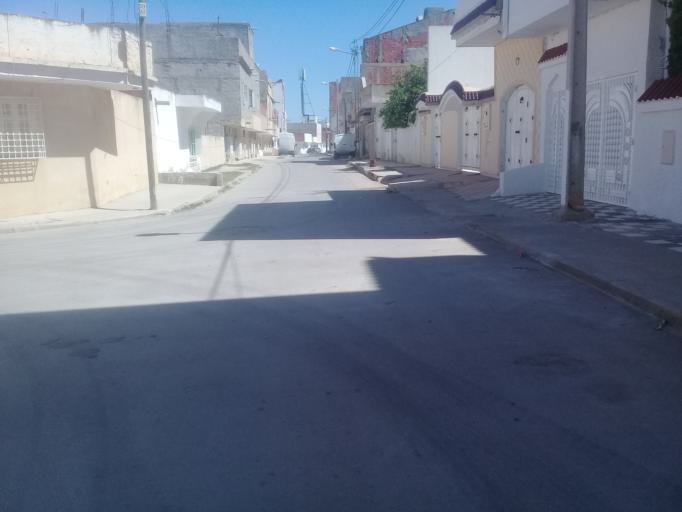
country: TN
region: Al Qayrawan
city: Kairouan
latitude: 35.6589
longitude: 10.1071
